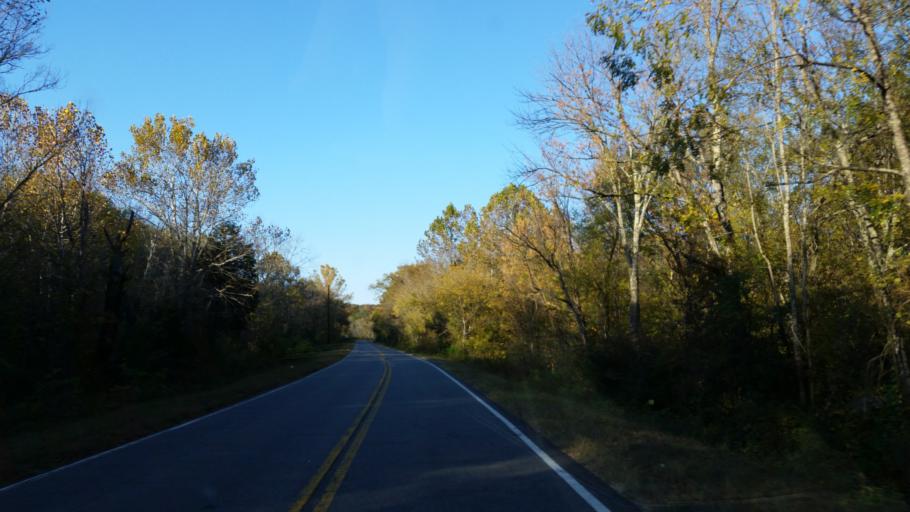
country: US
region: Georgia
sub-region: Bartow County
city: Adairsville
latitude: 34.2698
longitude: -84.9571
